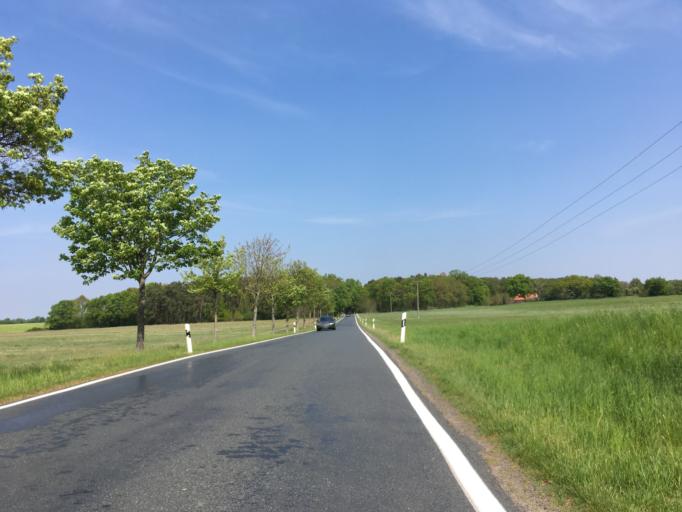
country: DE
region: Brandenburg
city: Melchow
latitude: 52.7206
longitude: 13.7129
